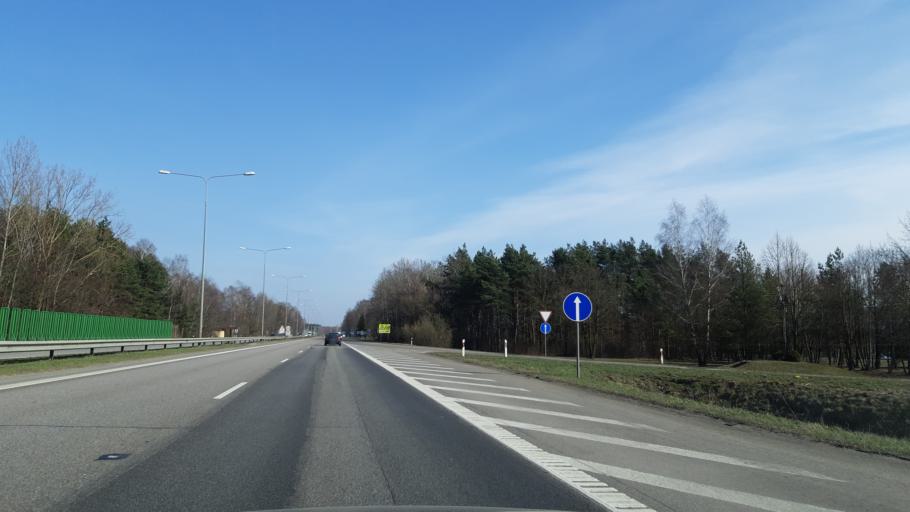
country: LT
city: Ramuciai
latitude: 54.9270
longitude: 24.0544
